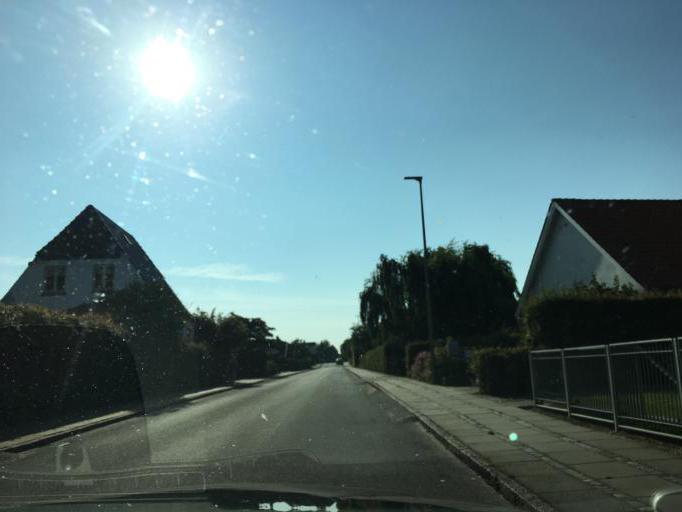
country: DK
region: South Denmark
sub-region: Kolding Kommune
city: Kolding
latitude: 55.4988
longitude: 9.4713
